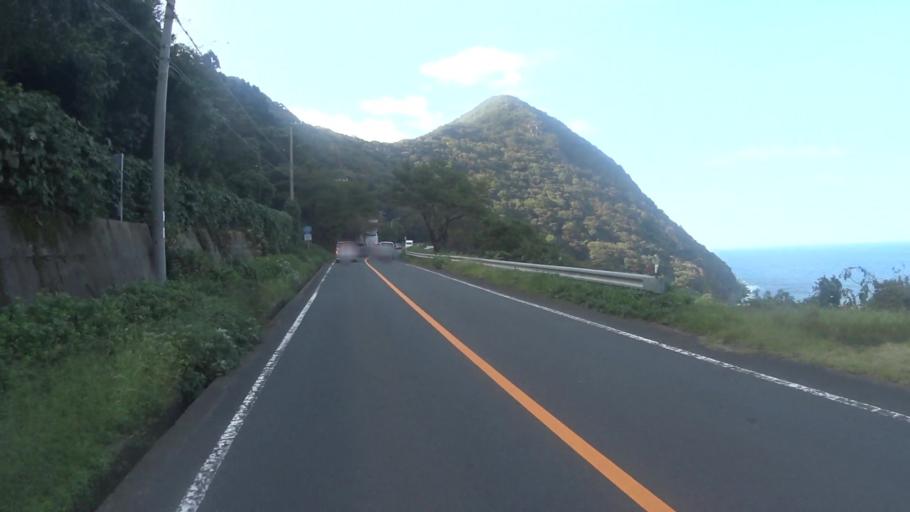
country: JP
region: Kyoto
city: Miyazu
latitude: 35.7498
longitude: 135.1409
